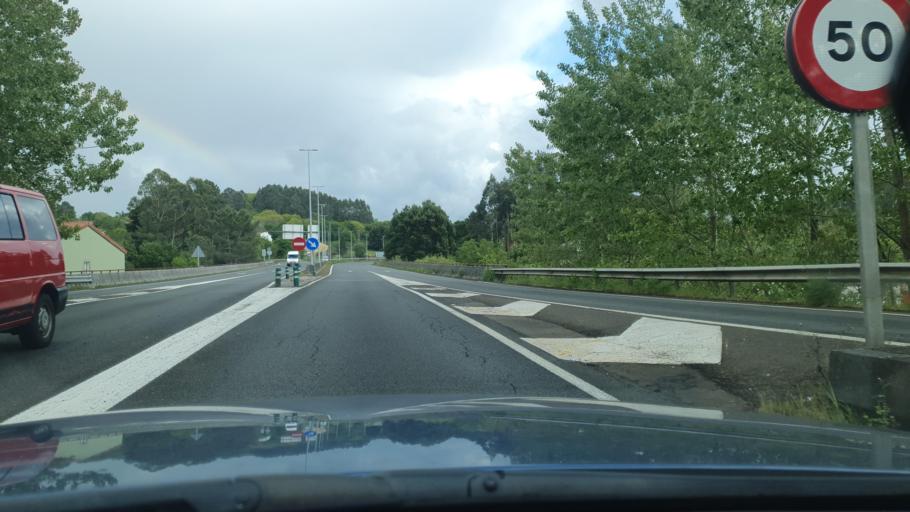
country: ES
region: Galicia
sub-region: Provincia da Coruna
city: Santiago de Compostela
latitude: 42.8687
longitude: -8.5748
